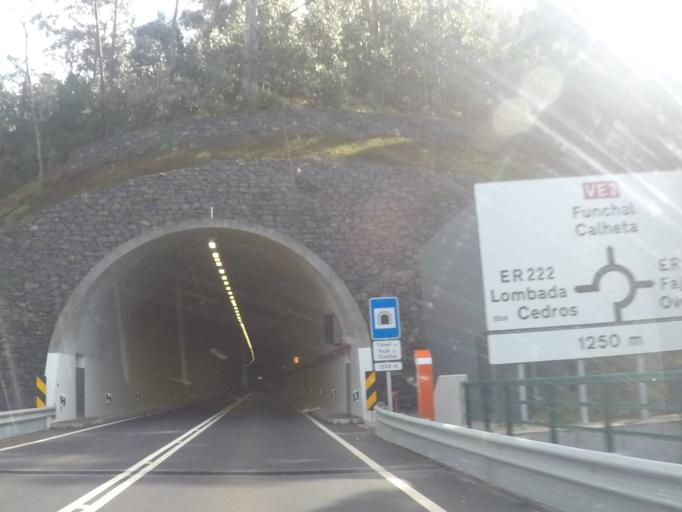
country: PT
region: Madeira
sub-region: Calheta
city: Faja da Ovelha
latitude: 32.7862
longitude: -17.2283
